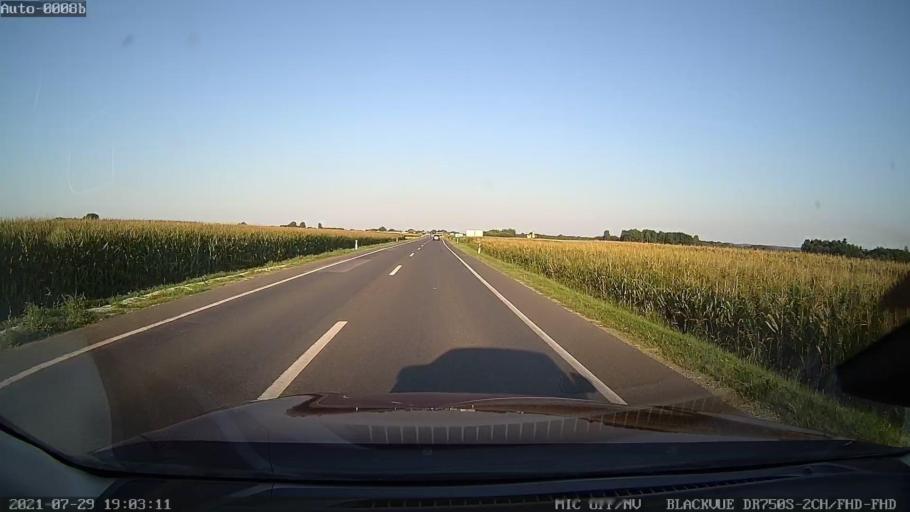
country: HR
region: Medimurska
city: Kursanec
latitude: 46.2983
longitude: 16.4173
